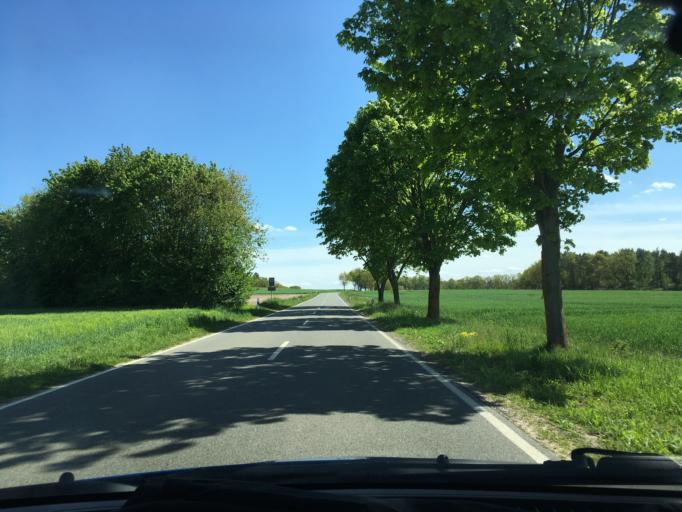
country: DE
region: Lower Saxony
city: Zernien
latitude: 53.0436
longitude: 10.8785
